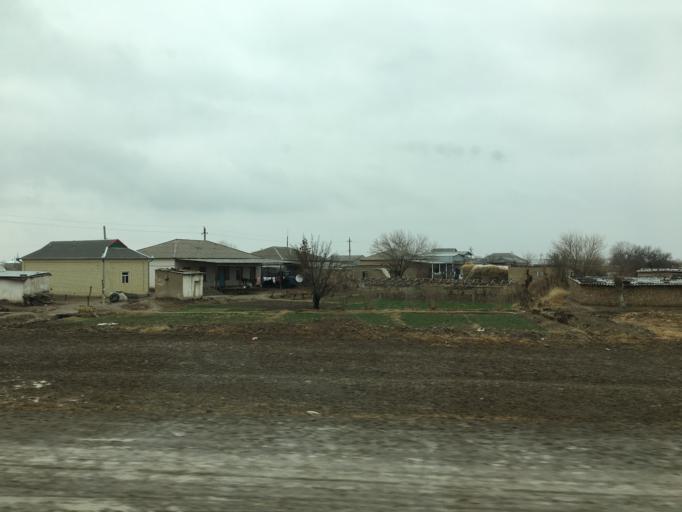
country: TM
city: Murgab
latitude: 37.4702
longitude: 62.0293
